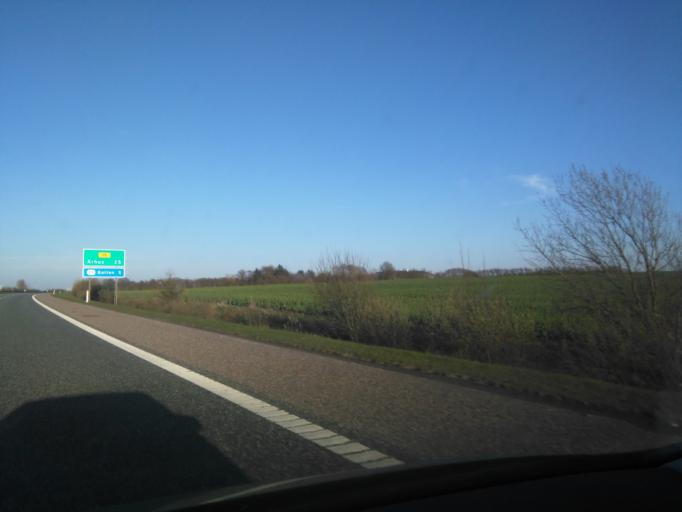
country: DK
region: Central Jutland
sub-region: Skanderborg Kommune
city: Galten
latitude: 56.1479
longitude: 9.8344
